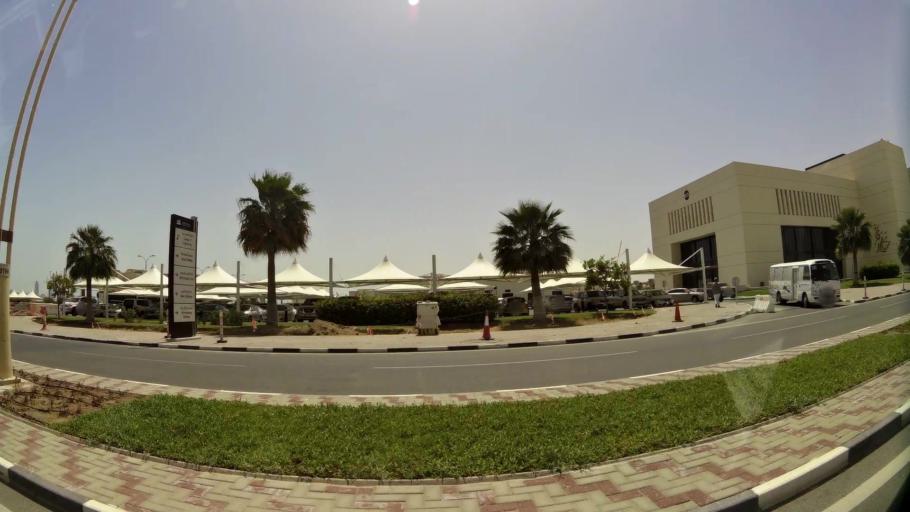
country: QA
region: Baladiyat Umm Salal
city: Umm Salal Muhammad
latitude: 25.3784
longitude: 51.4903
